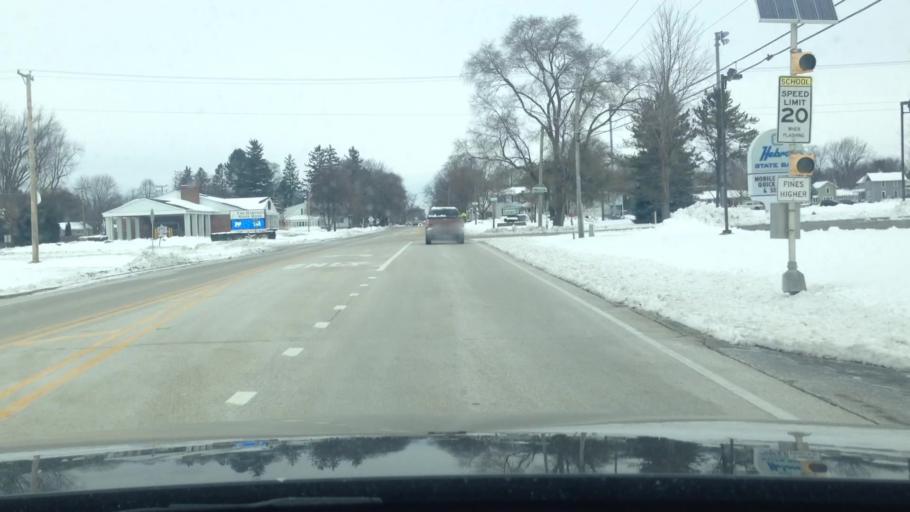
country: US
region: Illinois
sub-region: McHenry County
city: Hebron
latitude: 42.4644
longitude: -88.4328
